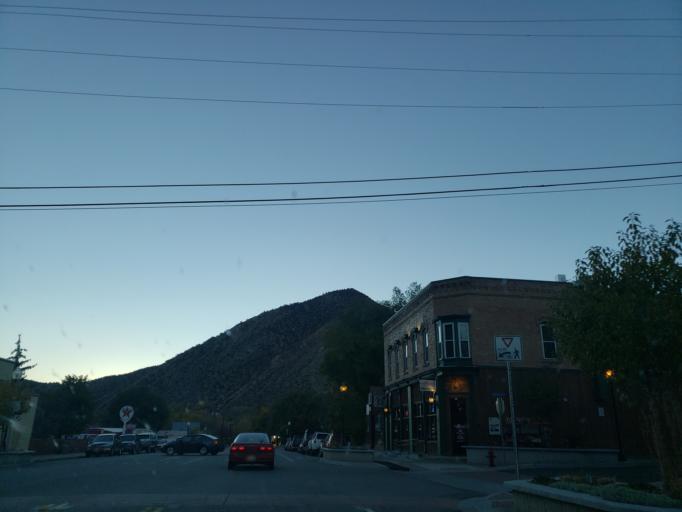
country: US
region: Colorado
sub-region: Garfield County
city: New Castle
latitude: 39.5715
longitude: -107.5352
